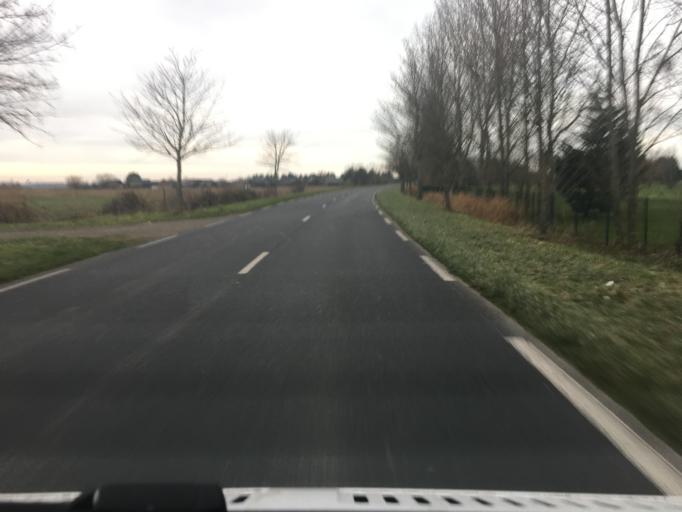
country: FR
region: Lower Normandy
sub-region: Departement du Calvados
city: Cabourg
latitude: 49.2745
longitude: -0.1254
